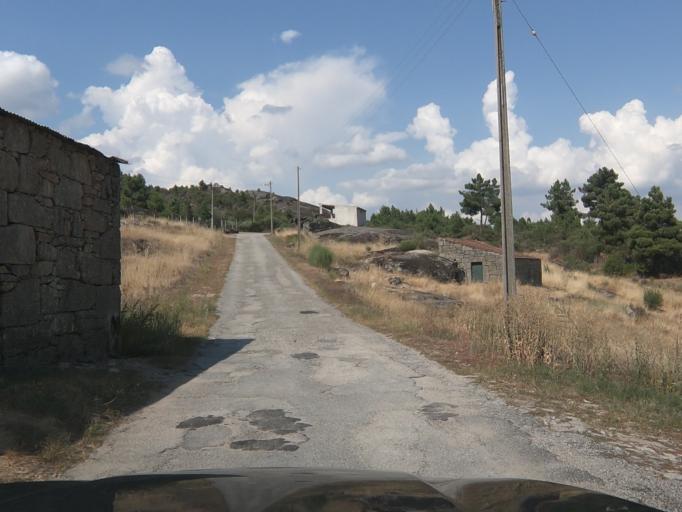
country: PT
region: Vila Real
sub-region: Sabrosa
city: Sabrosa
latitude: 41.3042
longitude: -7.5950
